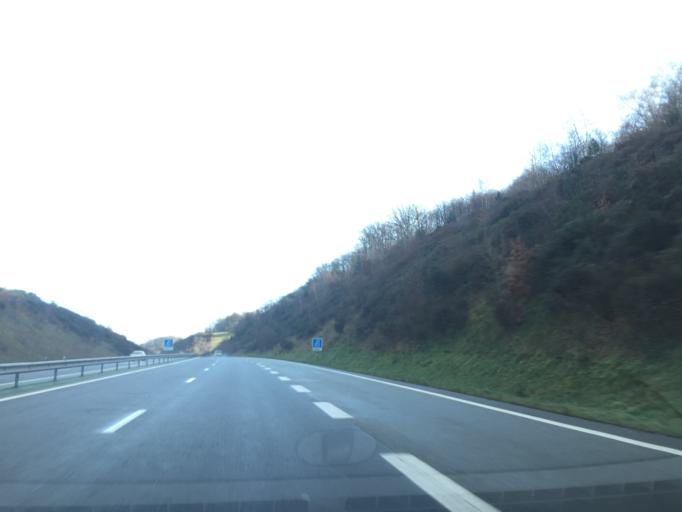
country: FR
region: Limousin
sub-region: Departement de la Correze
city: Saint-Mexant
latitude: 45.2906
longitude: 1.6335
